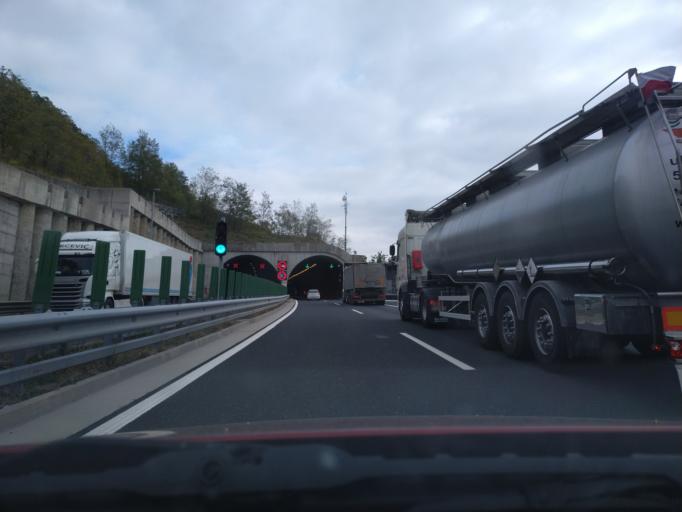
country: SI
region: Vipava
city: Vipava
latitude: 45.7731
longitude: 14.0243
